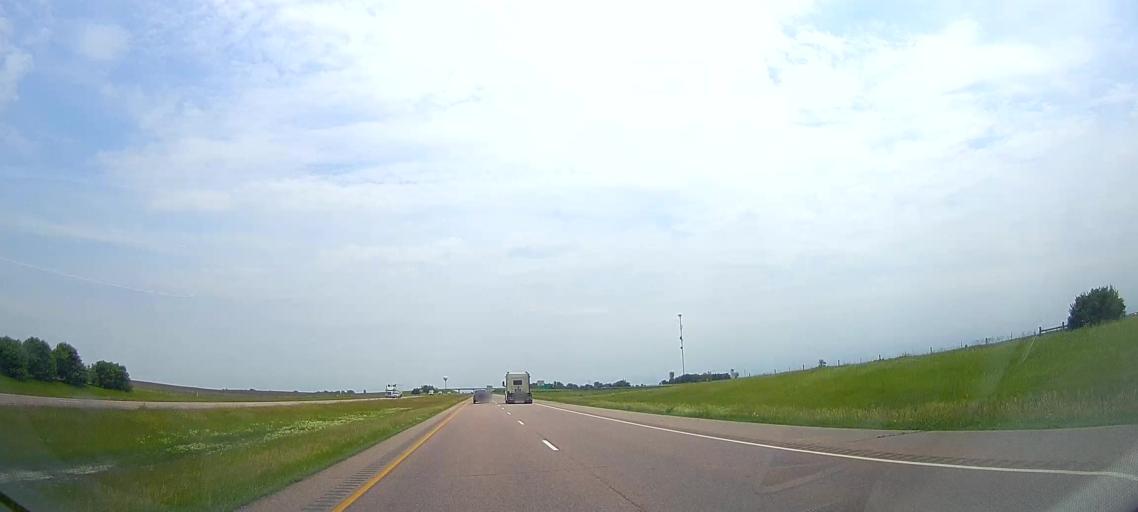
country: US
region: South Dakota
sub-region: Minnehaha County
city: Hartford
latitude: 43.6376
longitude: -97.0794
